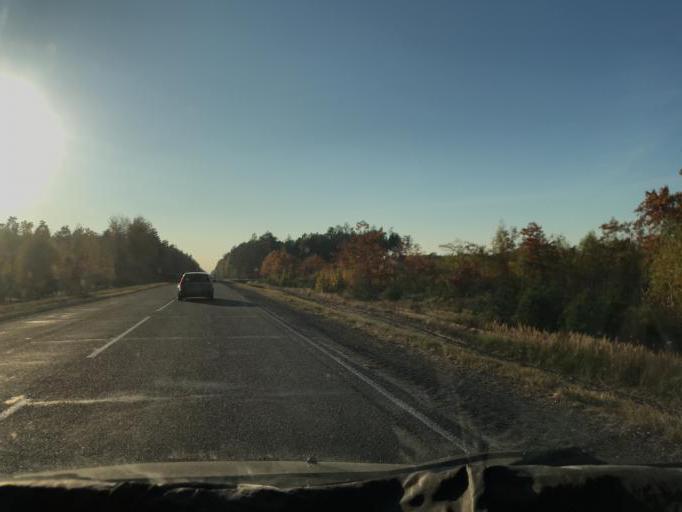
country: BY
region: Gomel
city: Zhytkavichy
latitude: 52.2693
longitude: 27.9749
